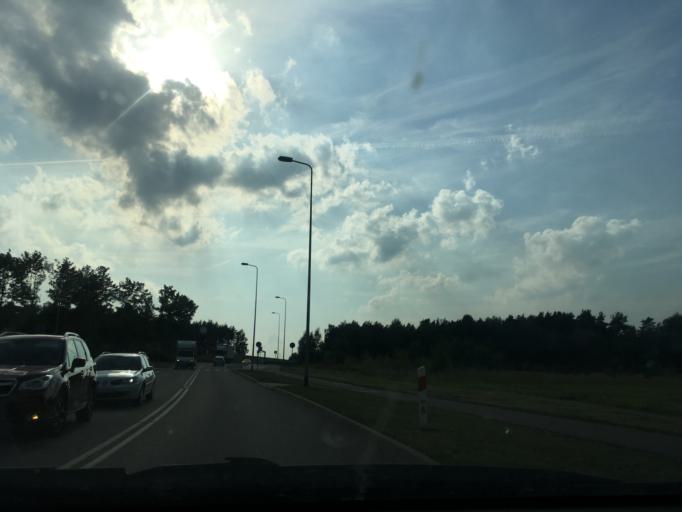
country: PL
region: Podlasie
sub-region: Powiat bialostocki
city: Choroszcz
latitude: 53.1505
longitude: 23.0528
